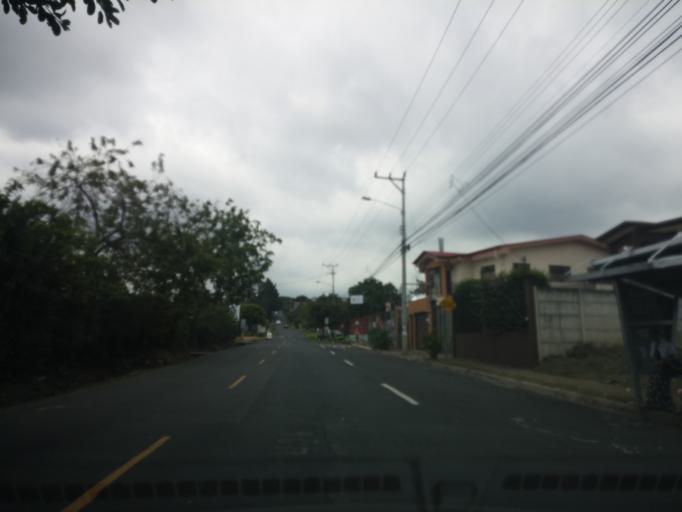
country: CR
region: Heredia
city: Llorente
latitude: 10.0085
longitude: -84.1521
